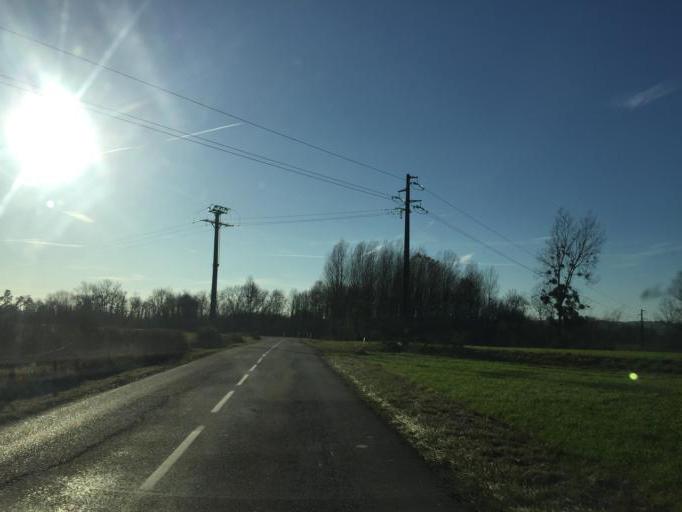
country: FR
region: Rhone-Alpes
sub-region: Departement de l'Ain
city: Chateau-Gaillard
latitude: 45.9614
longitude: 5.2908
